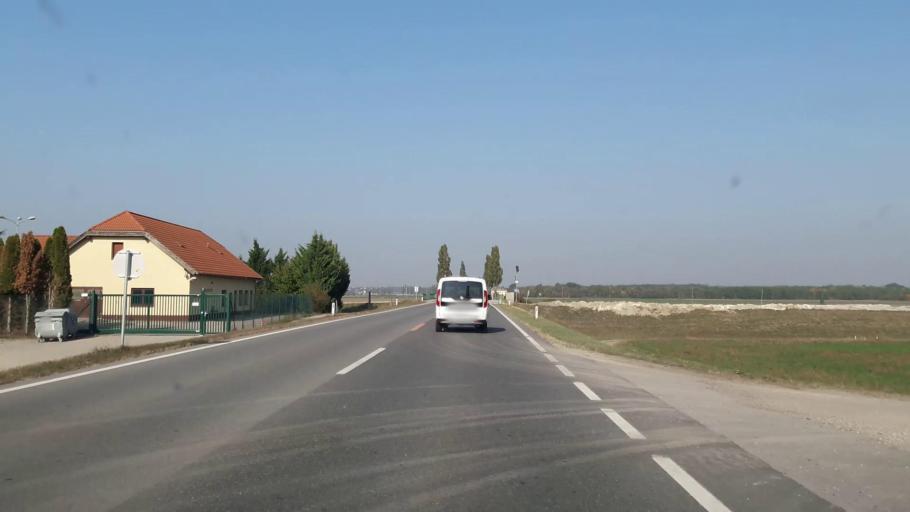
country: AT
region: Lower Austria
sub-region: Politischer Bezirk Ganserndorf
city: Engelhartstetten
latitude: 48.1866
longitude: 16.8950
